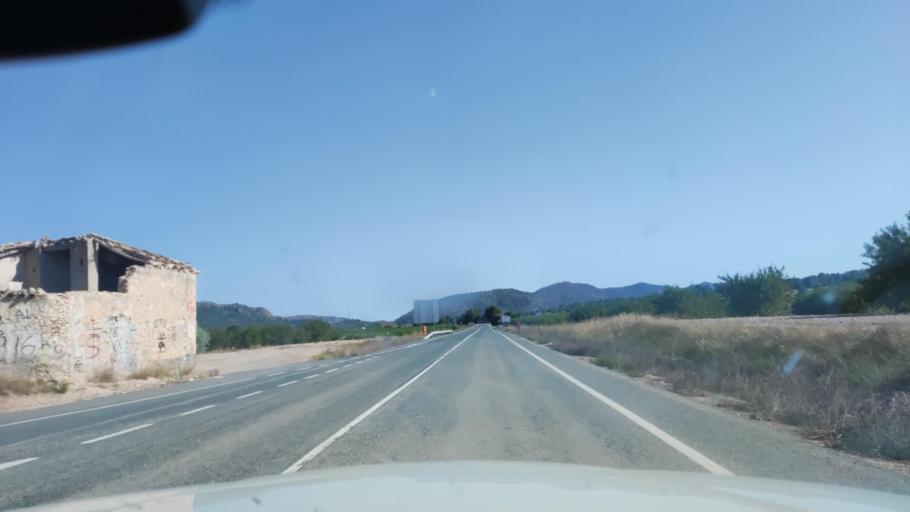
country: ES
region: Castille-La Mancha
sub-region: Provincia de Albacete
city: Tobarra
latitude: 38.6950
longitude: -1.6740
